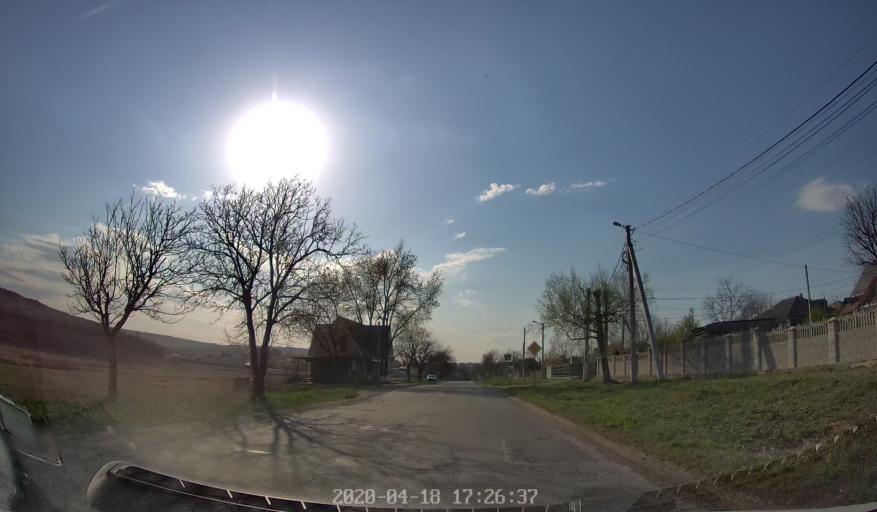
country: MD
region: Chisinau
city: Vadul lui Voda
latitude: 47.0655
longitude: 28.9891
